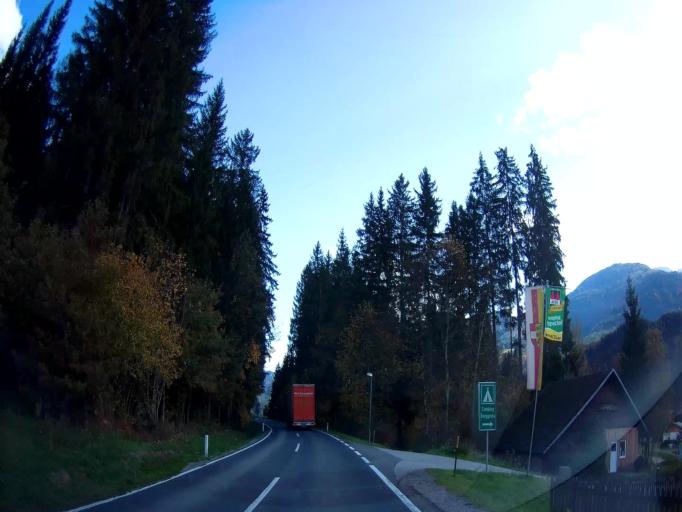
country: AT
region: Carinthia
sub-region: Politischer Bezirk Spittal an der Drau
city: Berg im Drautal
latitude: 46.7406
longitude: 13.1320
